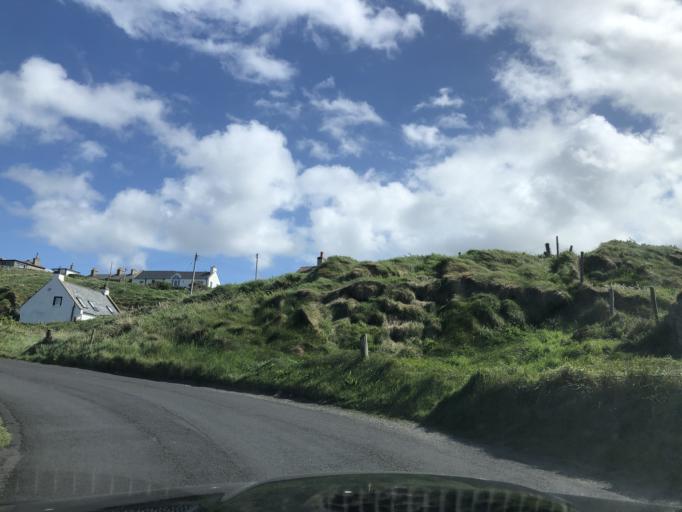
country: GB
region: Northern Ireland
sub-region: Moyle District
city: Ballycastle
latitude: 55.2439
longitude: -6.3685
